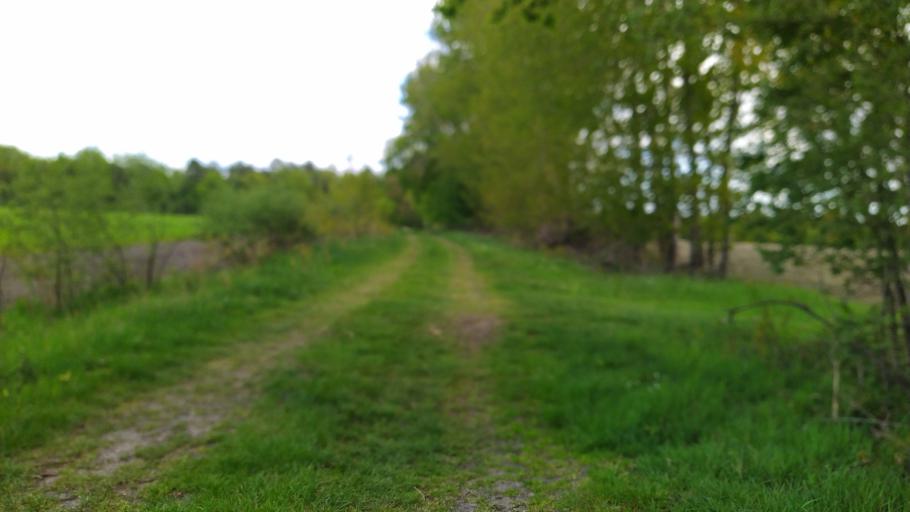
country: DE
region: Lower Saxony
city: Brest
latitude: 53.4153
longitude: 9.3848
